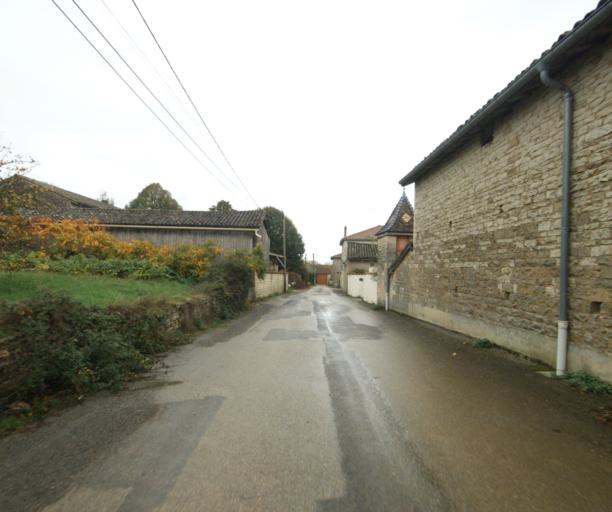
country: FR
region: Rhone-Alpes
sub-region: Departement de l'Ain
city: Pont-de-Vaux
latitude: 46.4827
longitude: 4.8656
